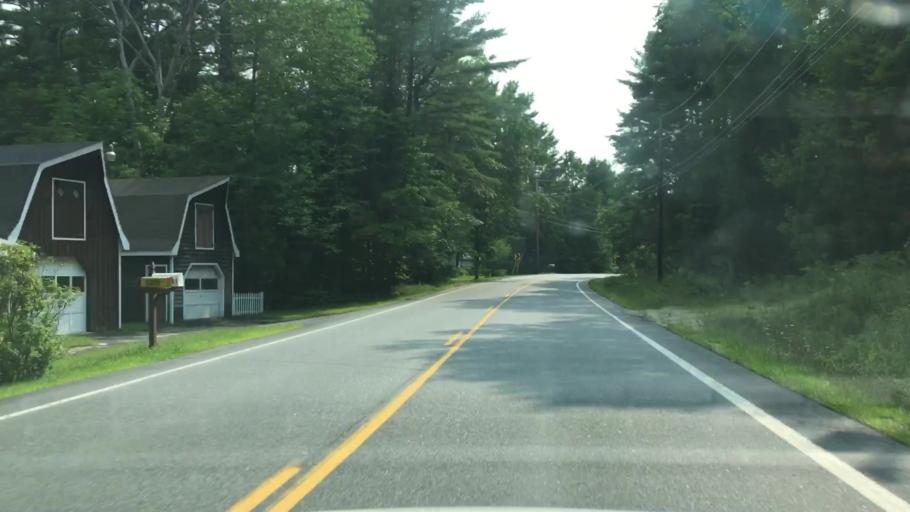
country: US
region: Maine
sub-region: Oxford County
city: South Paris
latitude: 44.2250
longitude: -70.4979
